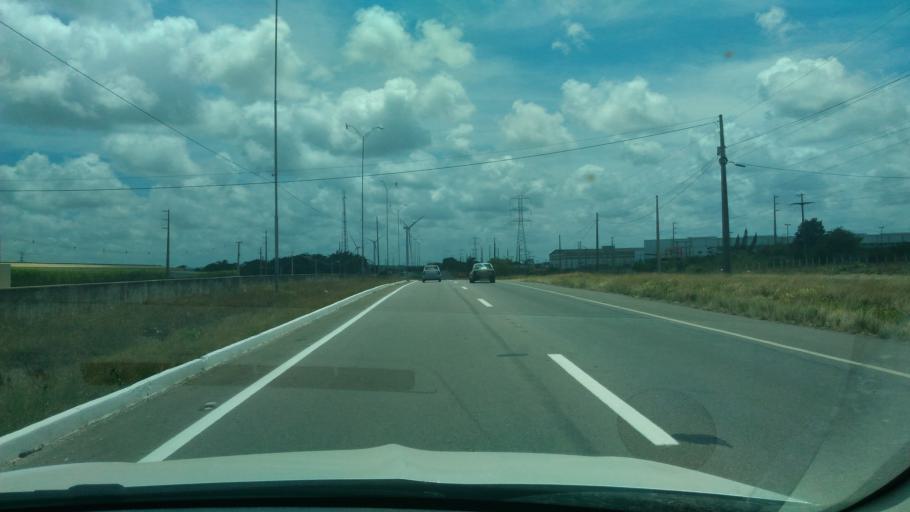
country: BR
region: Paraiba
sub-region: Conde
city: Conde
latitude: -7.2521
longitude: -34.9332
